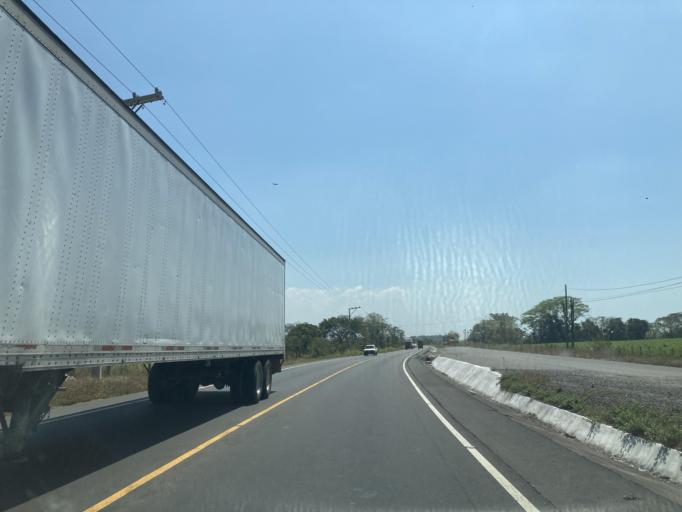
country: GT
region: Escuintla
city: Guanagazapa
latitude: 14.1036
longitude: -90.6189
